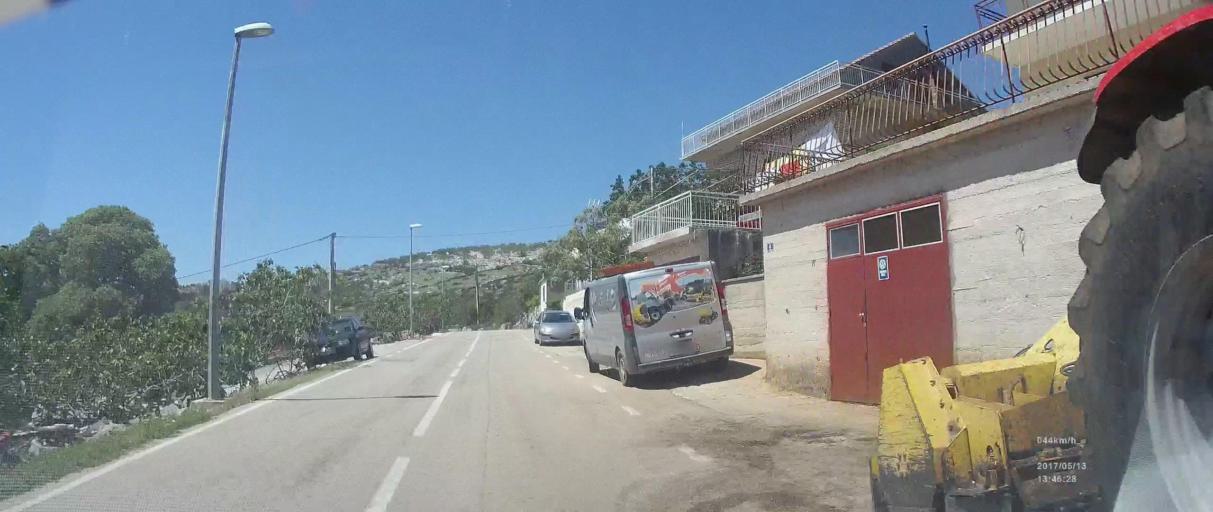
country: HR
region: Sibensko-Kniniska
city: Primosten
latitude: 43.6106
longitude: 15.9829
